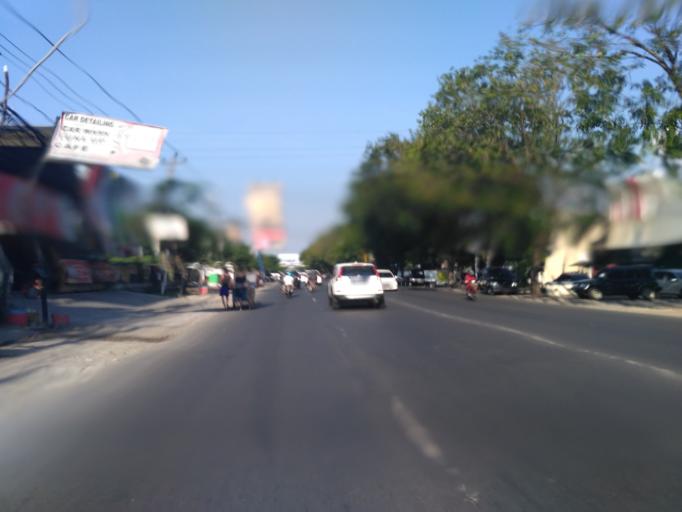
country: ID
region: Central Java
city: Semarang
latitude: -7.0083
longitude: 110.4633
